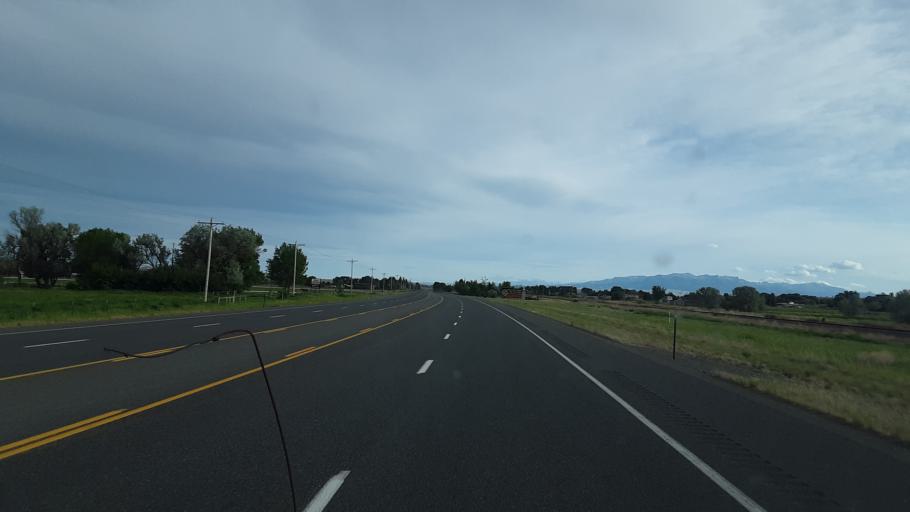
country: US
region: Wyoming
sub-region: Park County
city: Cody
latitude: 44.6036
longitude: -108.9640
